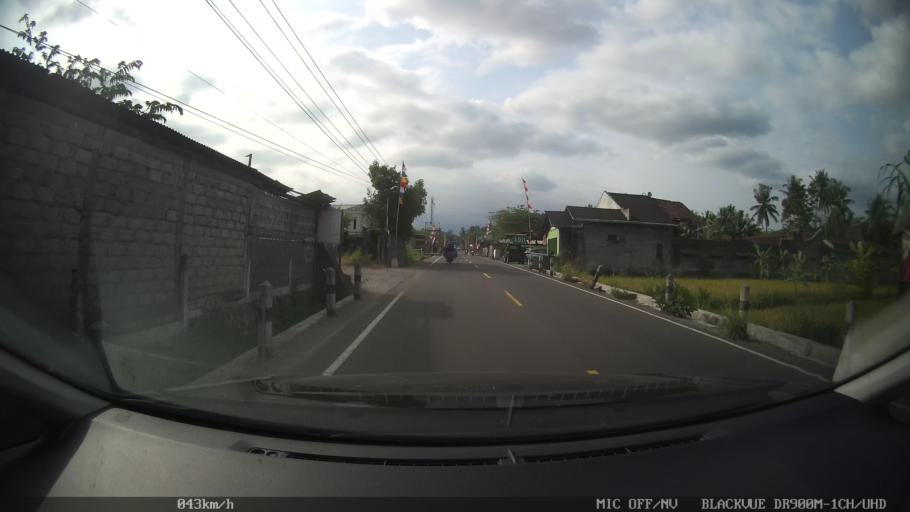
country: ID
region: Central Java
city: Candi Prambanan
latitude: -7.6861
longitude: 110.4613
